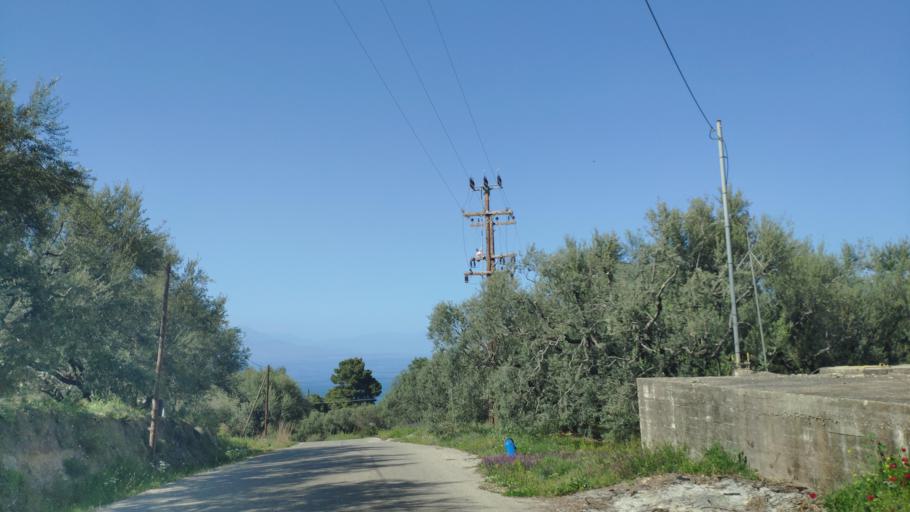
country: GR
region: West Greece
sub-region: Nomos Achaias
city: Aiyira
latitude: 38.1341
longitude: 22.3482
